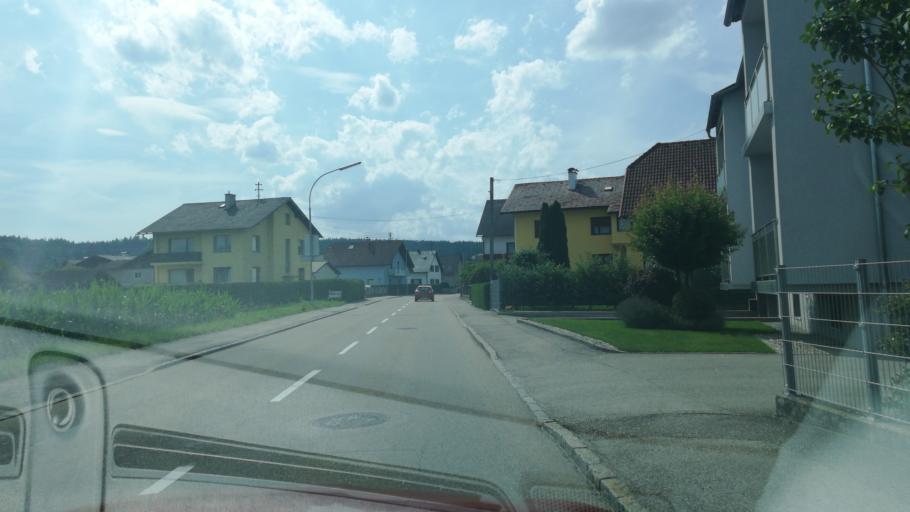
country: AT
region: Upper Austria
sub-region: Politischer Bezirk Vocklabruck
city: Attnang-Puchheim
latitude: 48.0175
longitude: 13.7188
